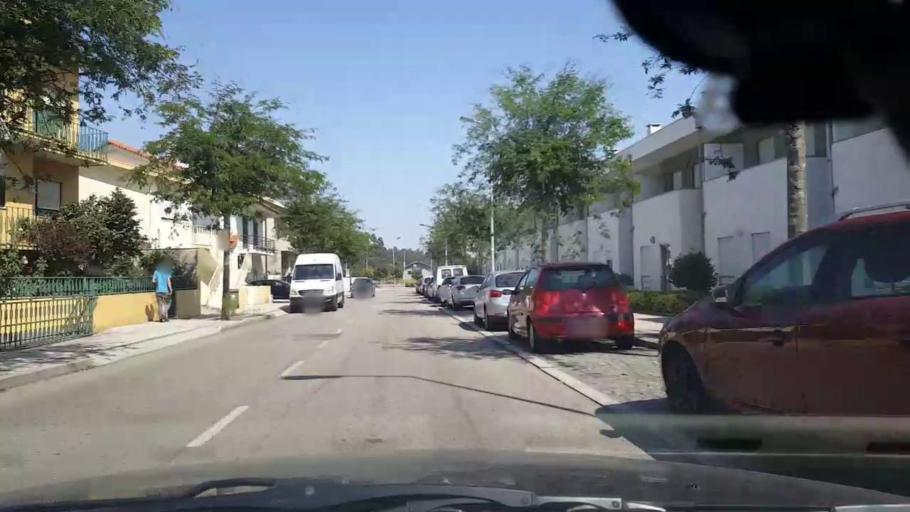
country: PT
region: Porto
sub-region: Vila do Conde
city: Vila do Conde
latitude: 41.3619
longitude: -8.7340
